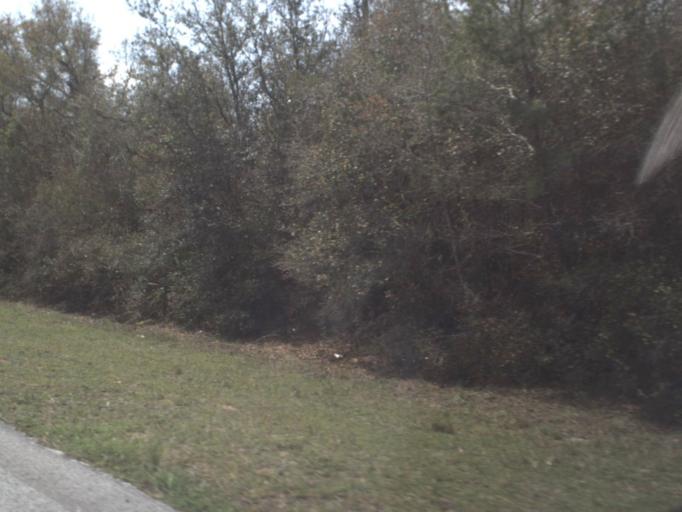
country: US
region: Florida
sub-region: Lake County
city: Astor
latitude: 29.1838
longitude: -81.6527
